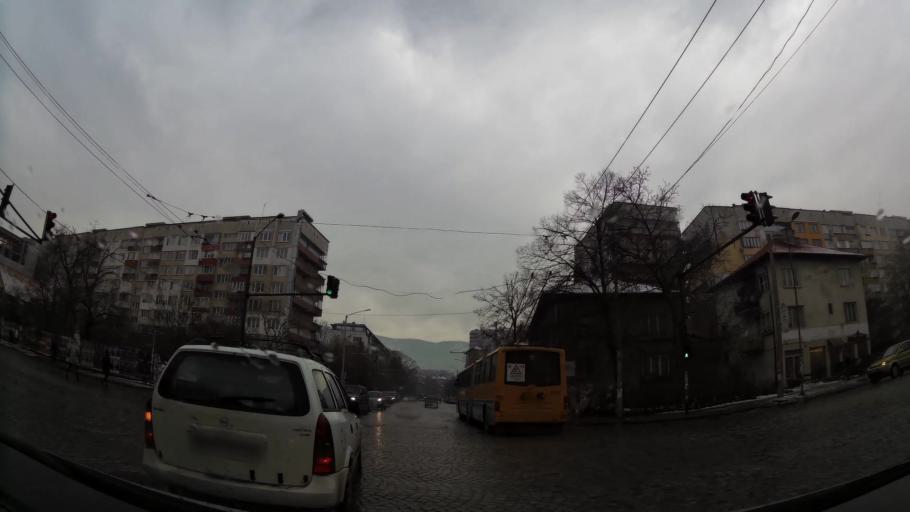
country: BG
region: Sofia-Capital
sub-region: Stolichna Obshtina
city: Sofia
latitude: 42.6761
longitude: 23.2887
